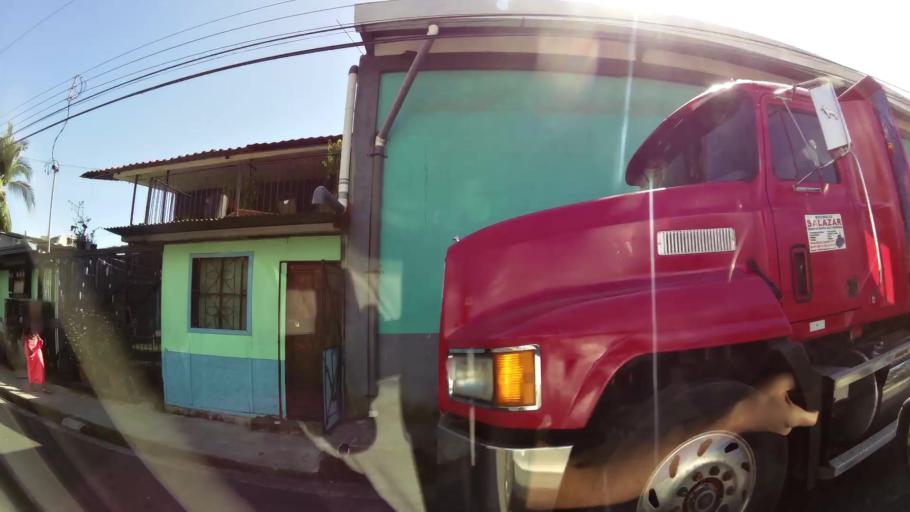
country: CR
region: Puntarenas
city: Quepos
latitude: 9.4323
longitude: -84.1614
